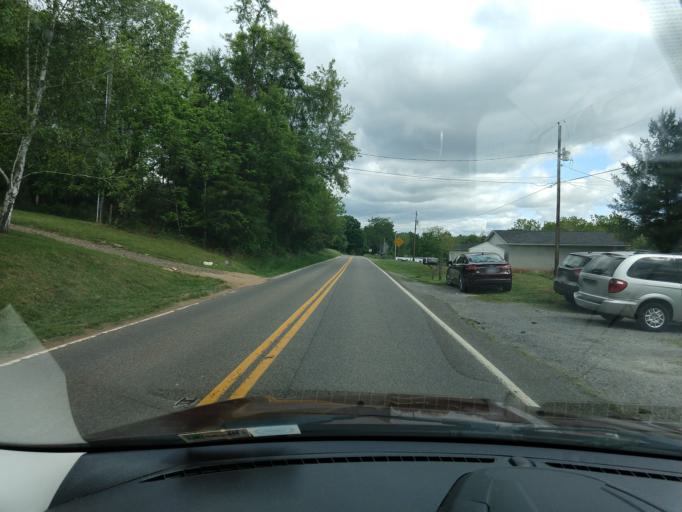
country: US
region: Virginia
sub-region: Carroll County
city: Woodlawn
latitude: 36.8327
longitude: -80.9540
